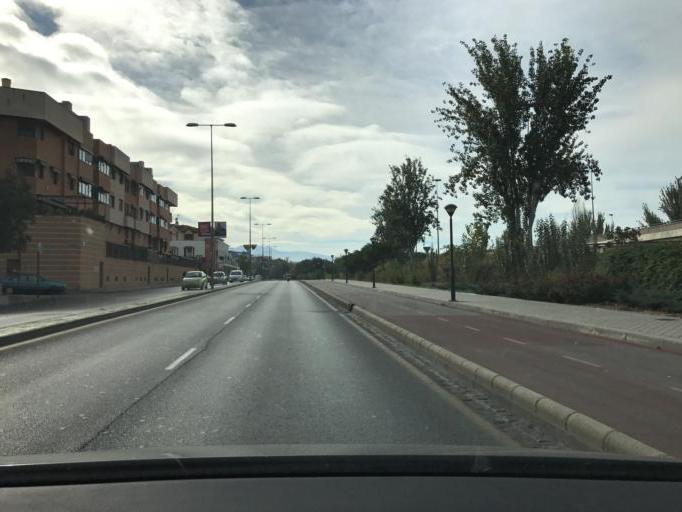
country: ES
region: Andalusia
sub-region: Provincia de Granada
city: Granada
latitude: 37.1668
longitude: -3.6095
